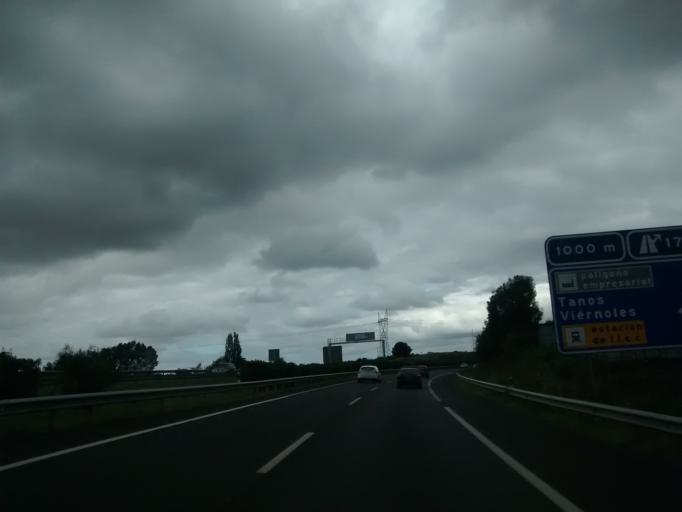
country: ES
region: Cantabria
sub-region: Provincia de Cantabria
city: Cartes
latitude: 43.3225
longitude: -4.0591
